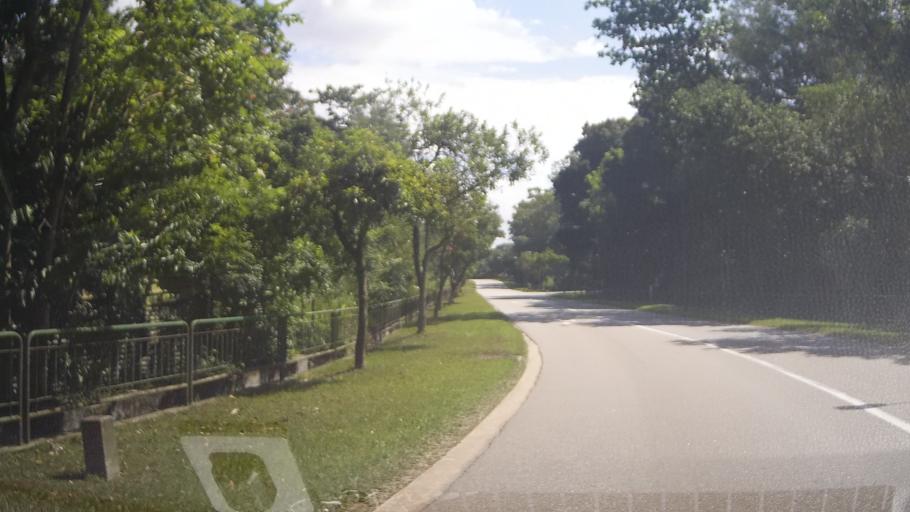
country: MY
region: Johor
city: Johor Bahru
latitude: 1.4278
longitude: 103.7075
